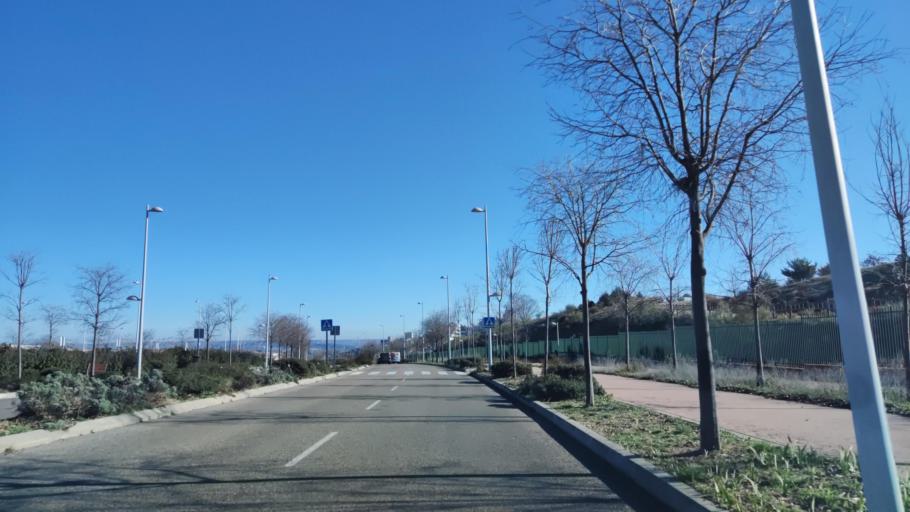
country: ES
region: Madrid
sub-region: Provincia de Madrid
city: Hortaleza
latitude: 40.4969
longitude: -3.6299
